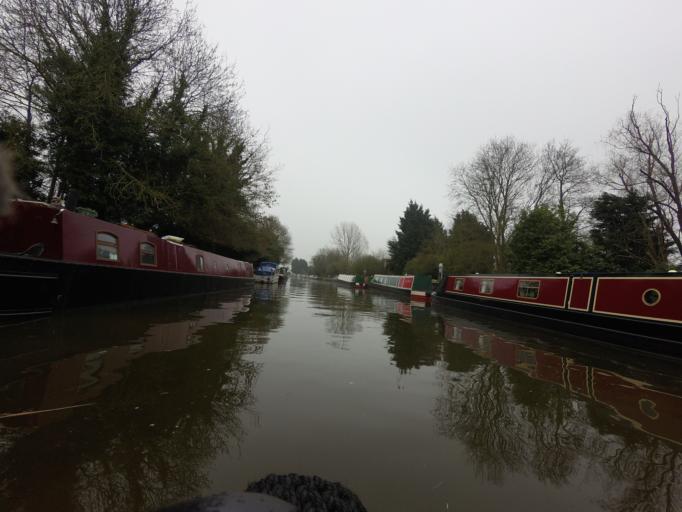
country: GB
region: England
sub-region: Hertfordshire
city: Tring
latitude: 51.7853
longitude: -0.6145
